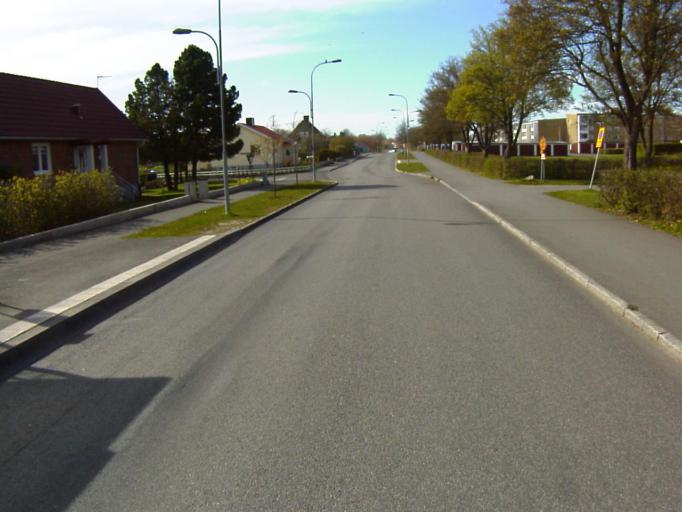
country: SE
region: Skane
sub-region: Kristianstads Kommun
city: Kristianstad
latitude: 56.0560
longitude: 14.1556
